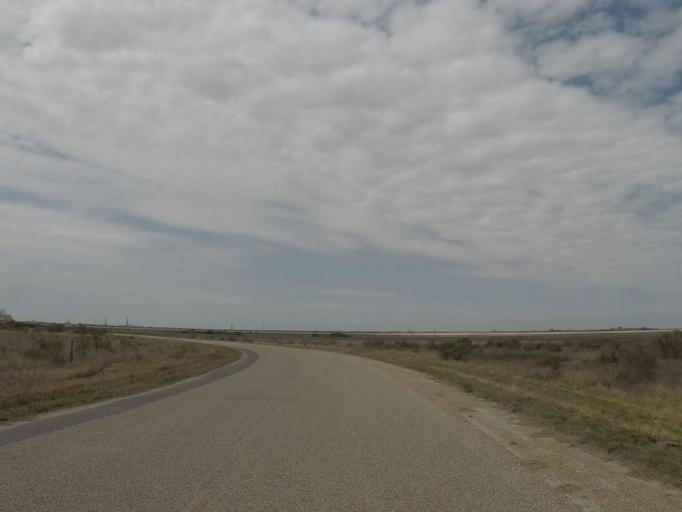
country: US
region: Texas
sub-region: Galveston County
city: Galveston
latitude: 29.3261
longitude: -94.7465
